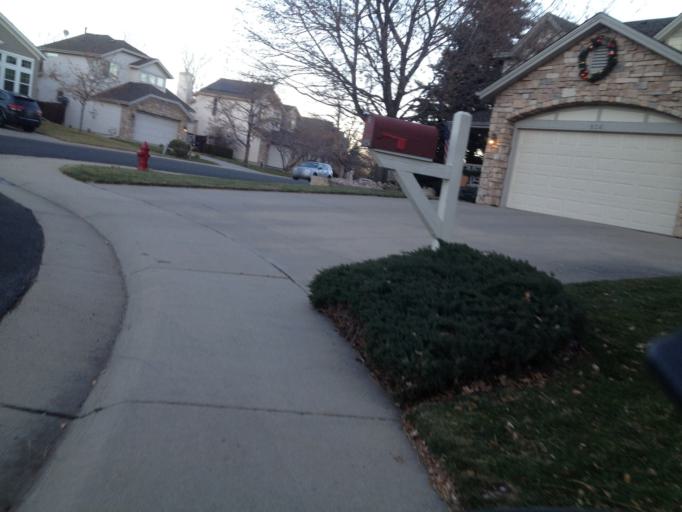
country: US
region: Colorado
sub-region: Boulder County
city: Superior
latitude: 39.9567
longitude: -105.1492
